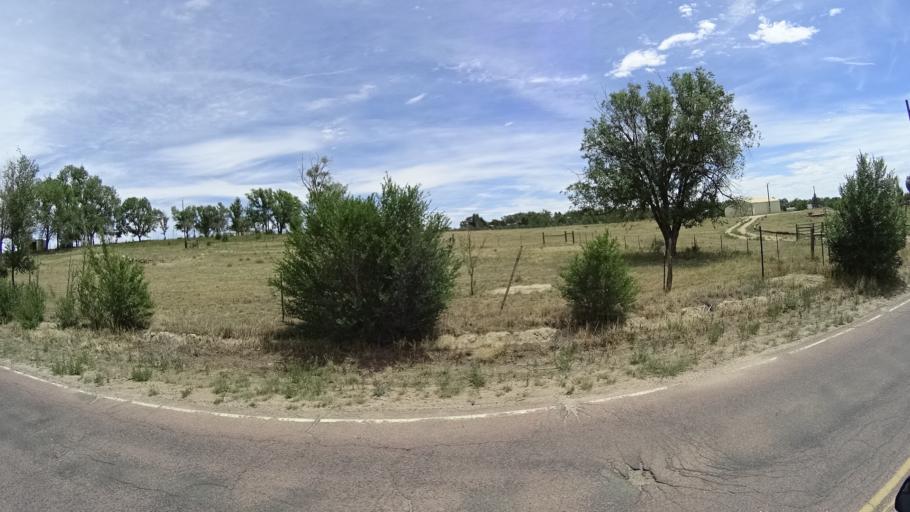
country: US
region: Colorado
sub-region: El Paso County
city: Fountain
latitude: 38.6805
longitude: -104.6736
